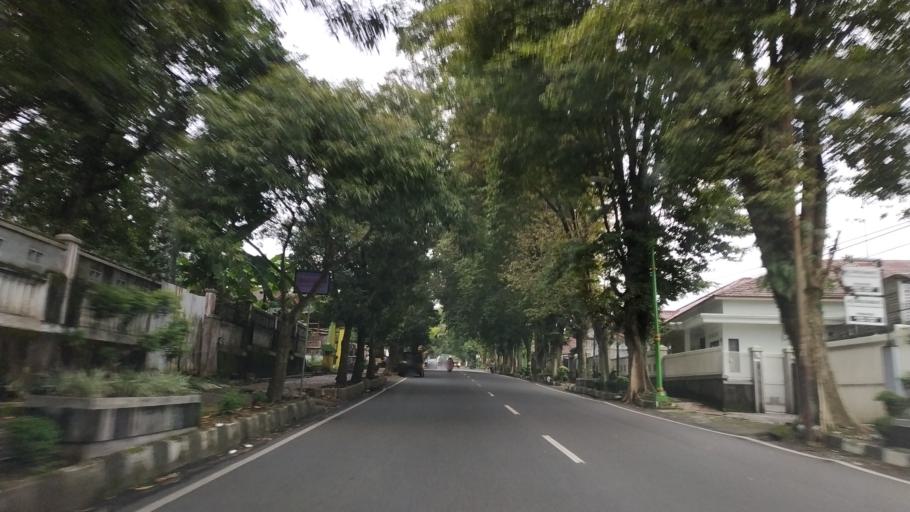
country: ID
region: Central Java
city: Salatiga
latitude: -7.3365
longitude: 110.5064
